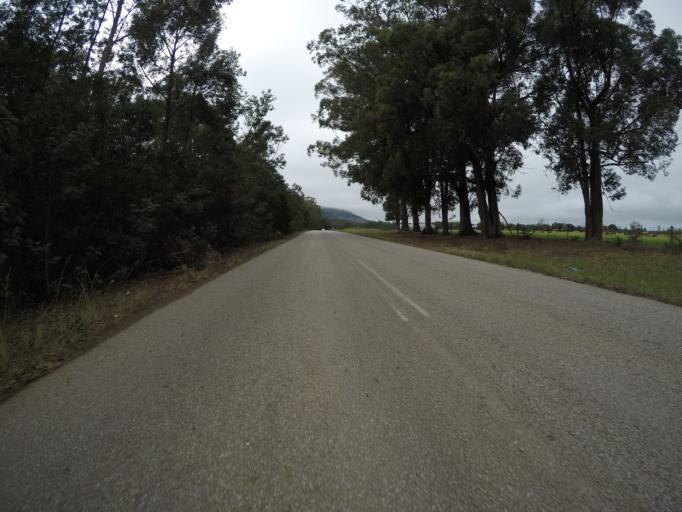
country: ZA
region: Eastern Cape
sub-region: Cacadu District Municipality
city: Kareedouw
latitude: -33.9815
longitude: 24.0438
